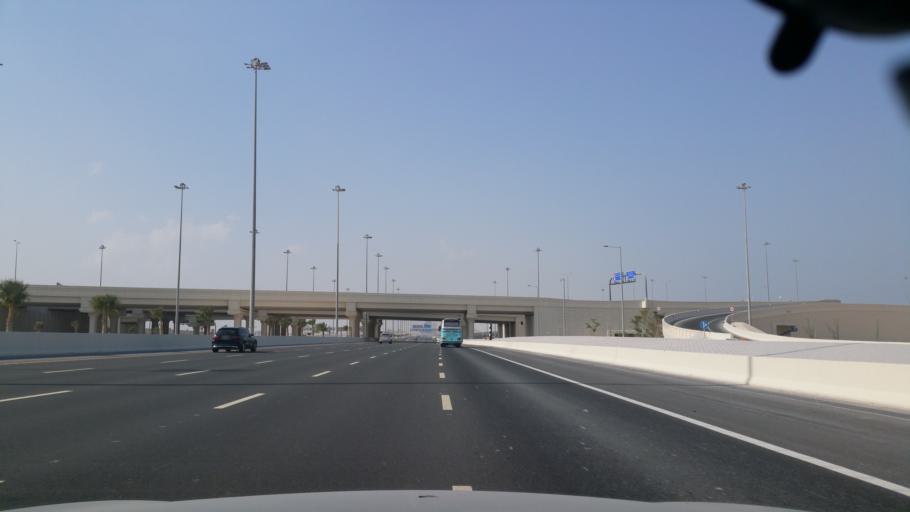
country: QA
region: Baladiyat Umm Salal
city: Umm Salal Muhammad
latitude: 25.4283
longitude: 51.4851
